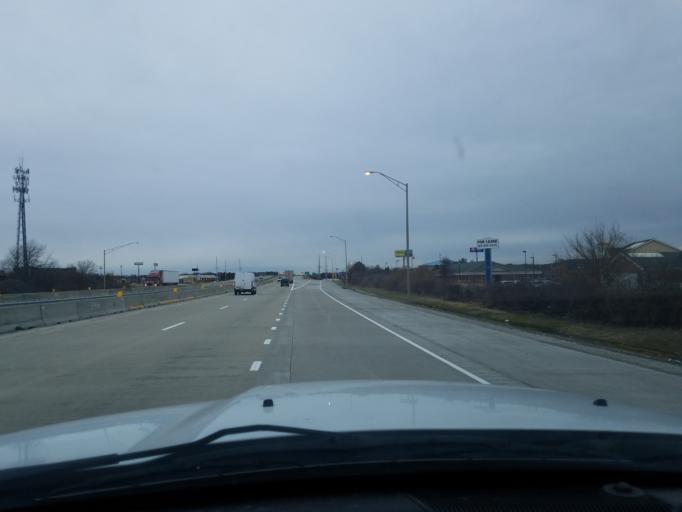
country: US
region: Indiana
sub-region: Tippecanoe County
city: Lafayette
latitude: 40.4147
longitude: -86.8178
